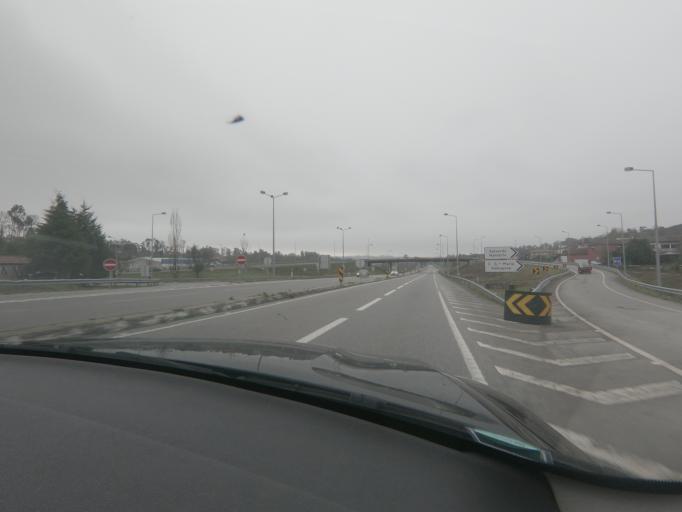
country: PT
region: Viseu
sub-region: Concelho de Tondela
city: Tondela
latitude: 40.5369
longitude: -8.0580
